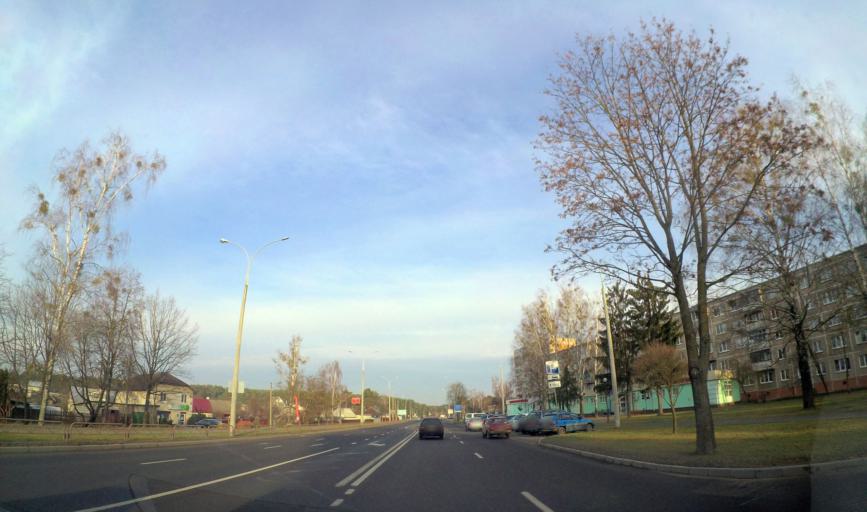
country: BY
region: Grodnenskaya
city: Hrodna
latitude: 53.6706
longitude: 23.7918
